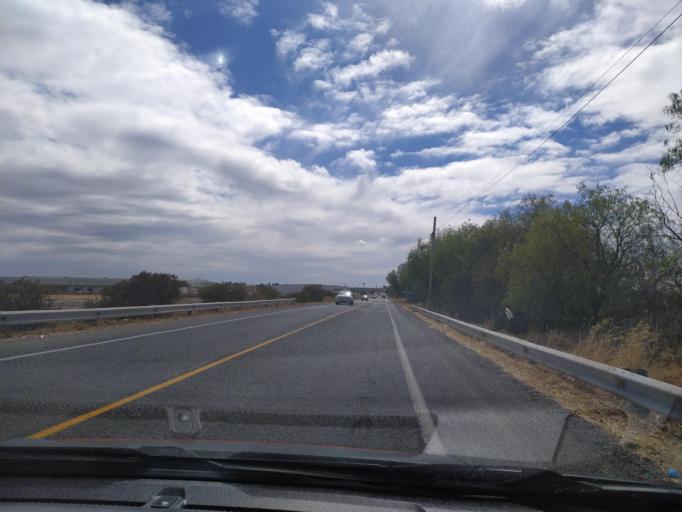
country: LA
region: Oudomxai
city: Muang La
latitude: 21.0085
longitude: 101.8297
